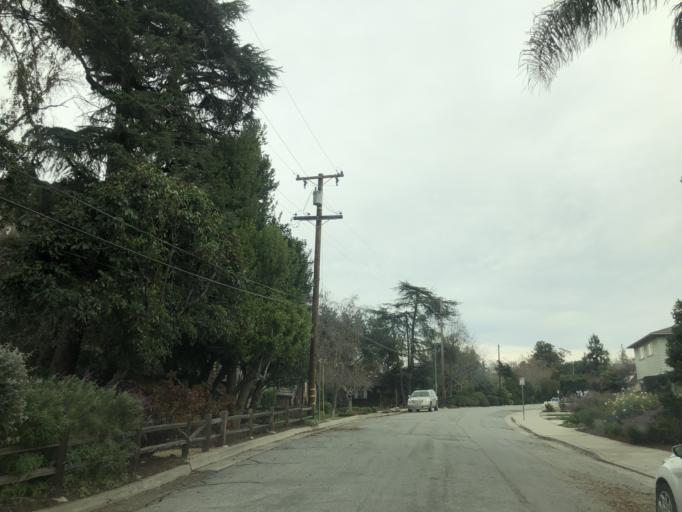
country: US
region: California
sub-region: Santa Clara County
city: San Jose
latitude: 37.3421
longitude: -121.8720
